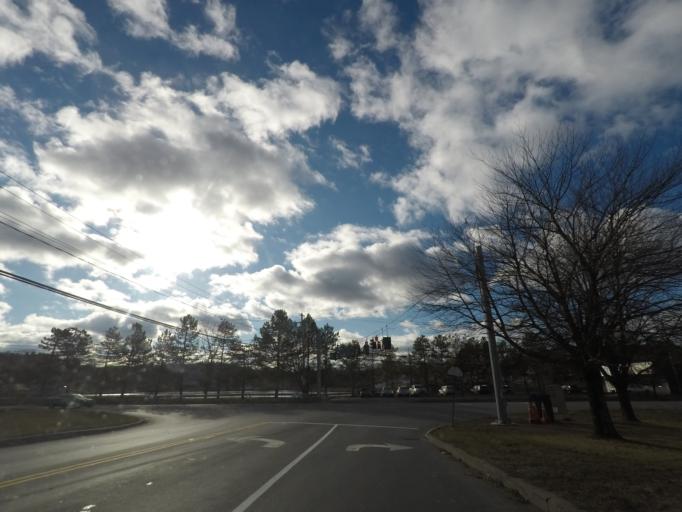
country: US
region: New York
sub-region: Saratoga County
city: Waterford
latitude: 42.7851
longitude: -73.6526
